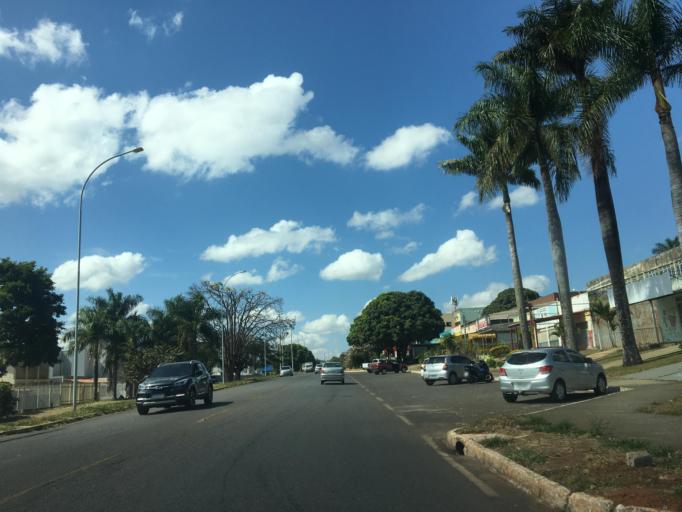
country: BR
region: Federal District
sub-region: Brasilia
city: Brasilia
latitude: -15.6456
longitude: -47.7903
